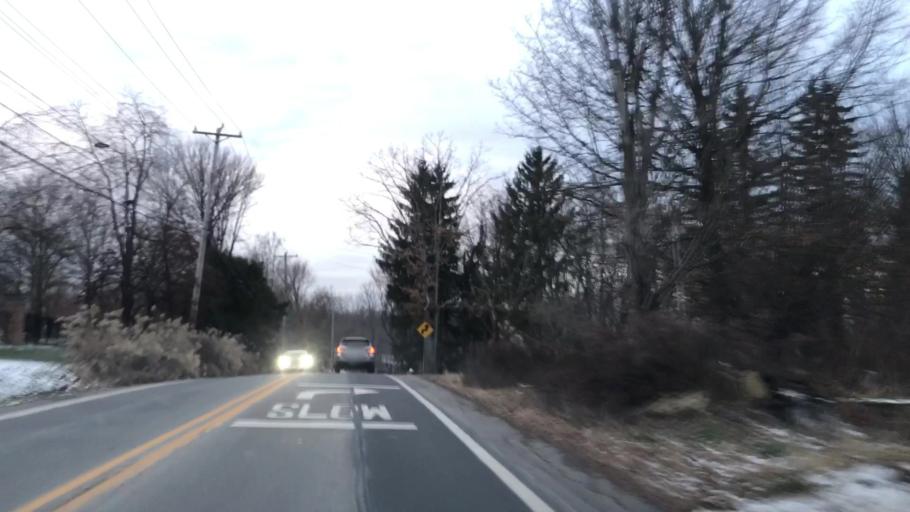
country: US
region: Pennsylvania
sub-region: Allegheny County
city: Gibsonia
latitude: 40.6348
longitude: -80.0058
